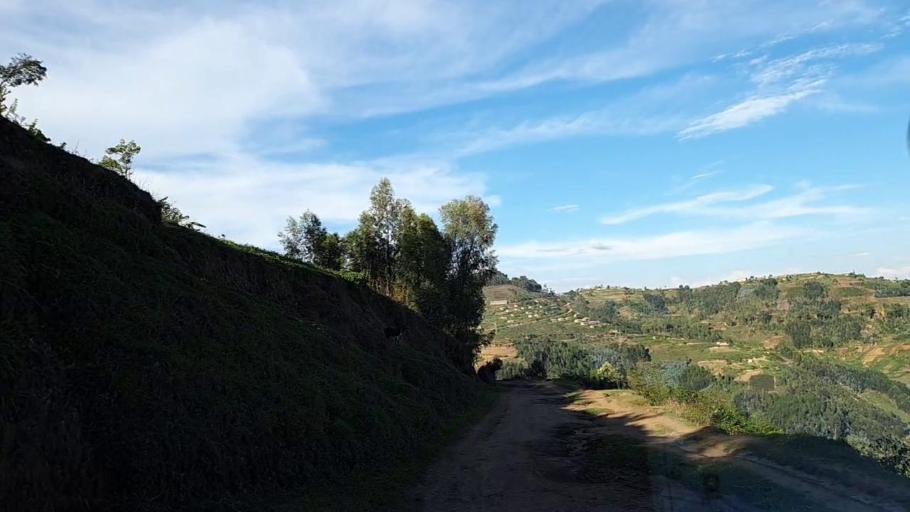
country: RW
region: Southern Province
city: Gikongoro
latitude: -2.4100
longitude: 29.5225
